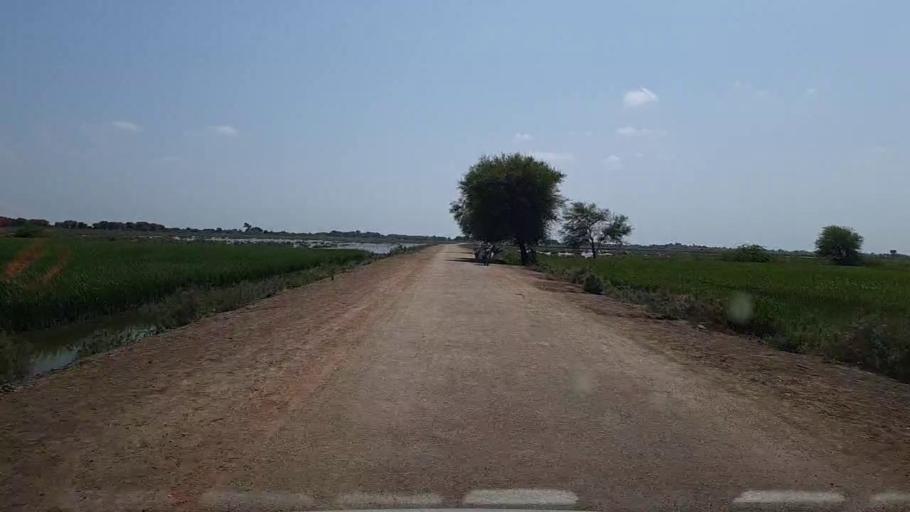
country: PK
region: Sindh
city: Kario
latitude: 24.8362
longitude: 68.7030
